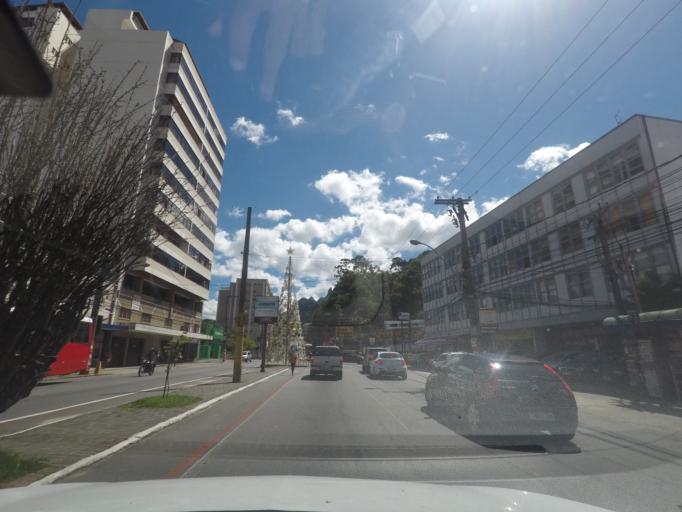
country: BR
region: Rio de Janeiro
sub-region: Teresopolis
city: Teresopolis
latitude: -22.4227
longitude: -42.9770
